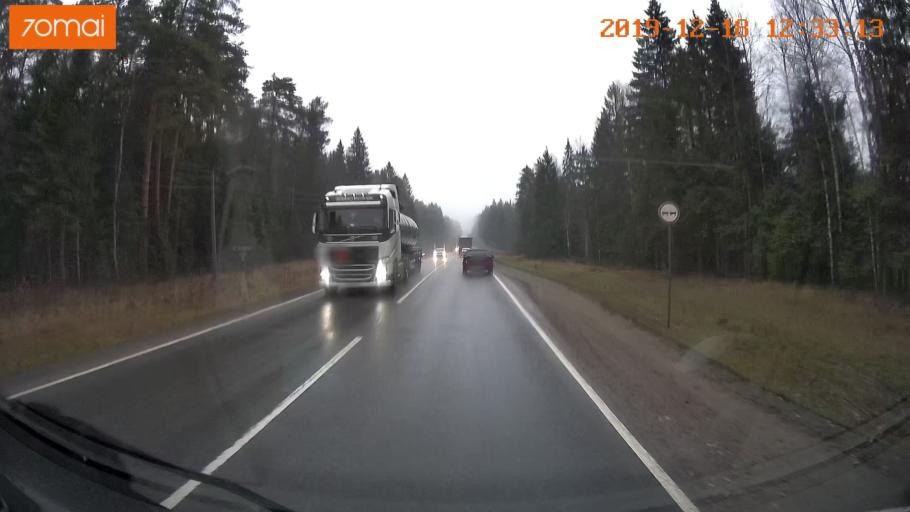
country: RU
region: Moskovskaya
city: Rumyantsevo
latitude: 56.1111
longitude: 36.5586
